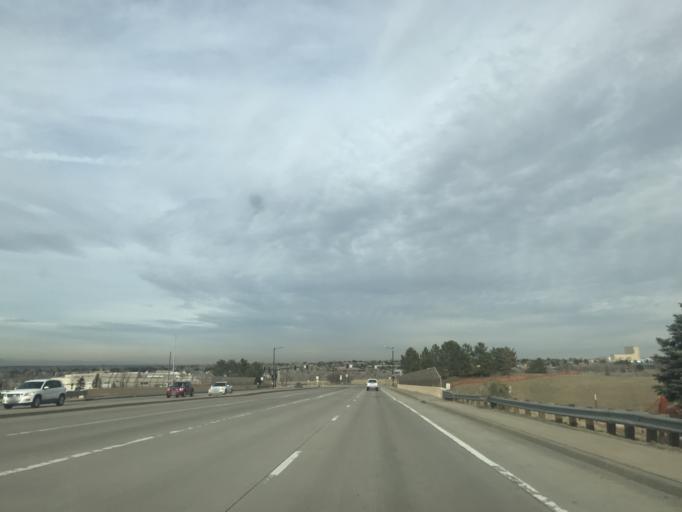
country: US
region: Colorado
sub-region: Douglas County
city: Highlands Ranch
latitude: 39.5590
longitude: -105.0080
